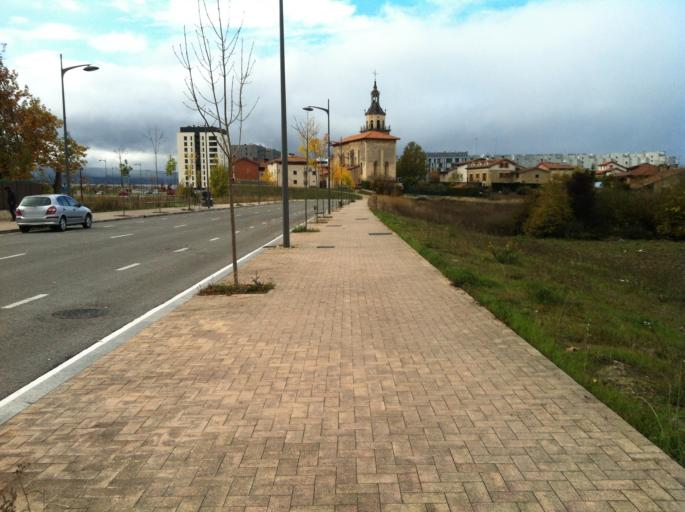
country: ES
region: Basque Country
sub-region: Provincia de Alava
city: Gasteiz / Vitoria
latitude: 42.8509
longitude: -2.7031
